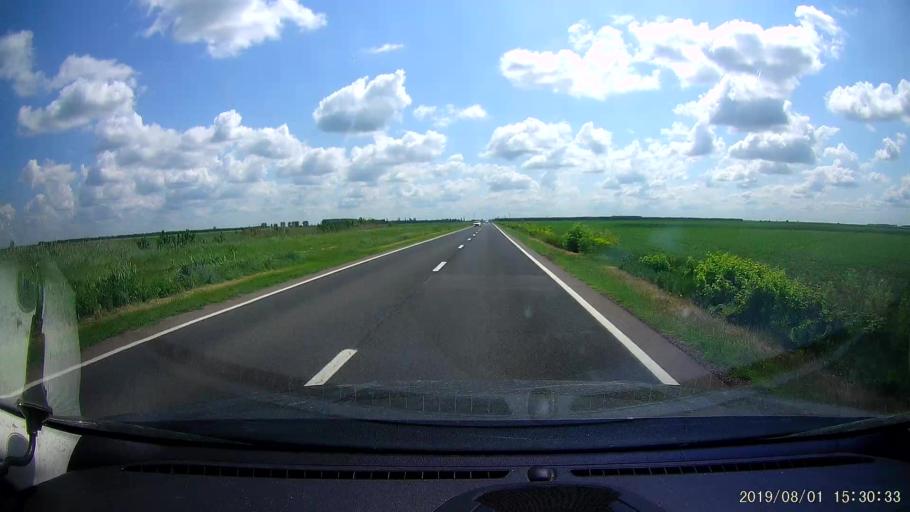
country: RO
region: Braila
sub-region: Comuna Viziru
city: Viziru
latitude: 44.9617
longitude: 27.6756
